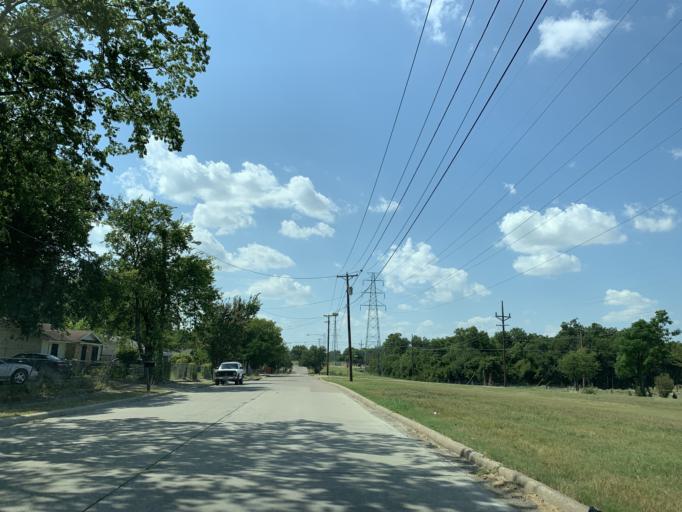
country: US
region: Texas
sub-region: Dallas County
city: Hutchins
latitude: 32.7066
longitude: -96.7681
